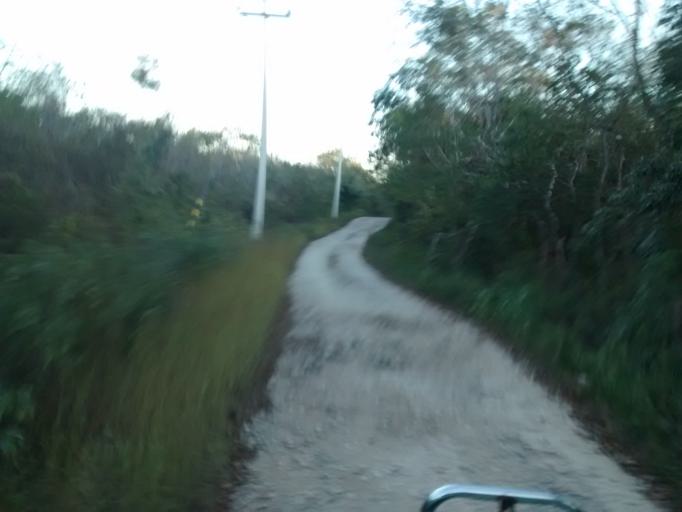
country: MX
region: Yucatan
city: Chichimila
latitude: 20.4466
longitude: -88.1962
